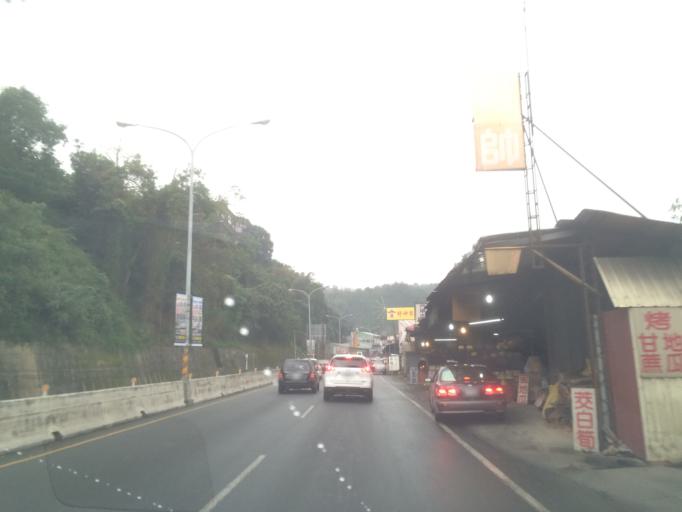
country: TW
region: Taiwan
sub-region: Nantou
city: Puli
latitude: 23.9660
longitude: 120.9427
